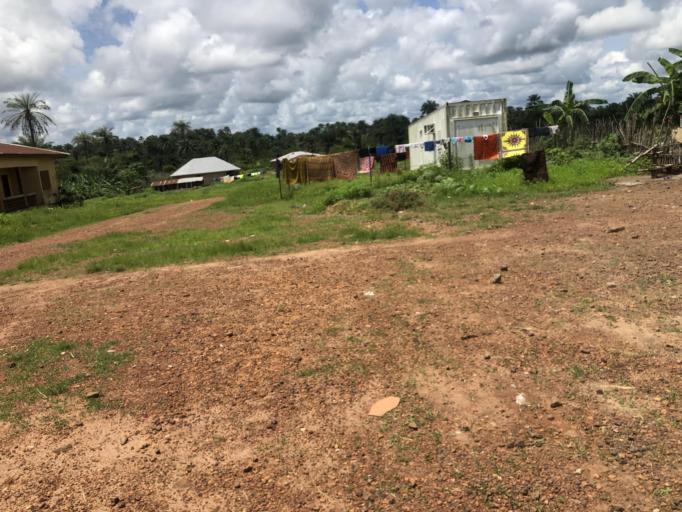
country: SL
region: Northern Province
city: Port Loko
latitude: 8.7181
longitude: -12.8480
